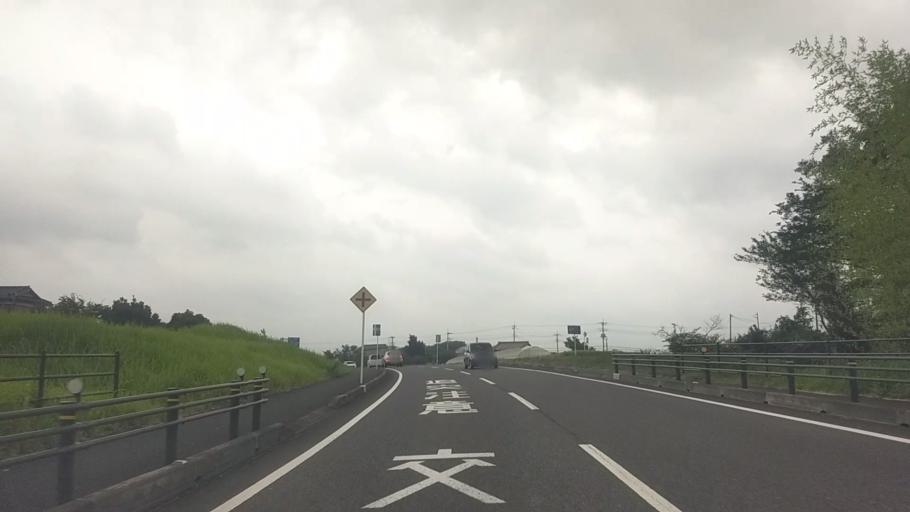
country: JP
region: Chiba
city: Kisarazu
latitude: 35.3155
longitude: 140.0548
